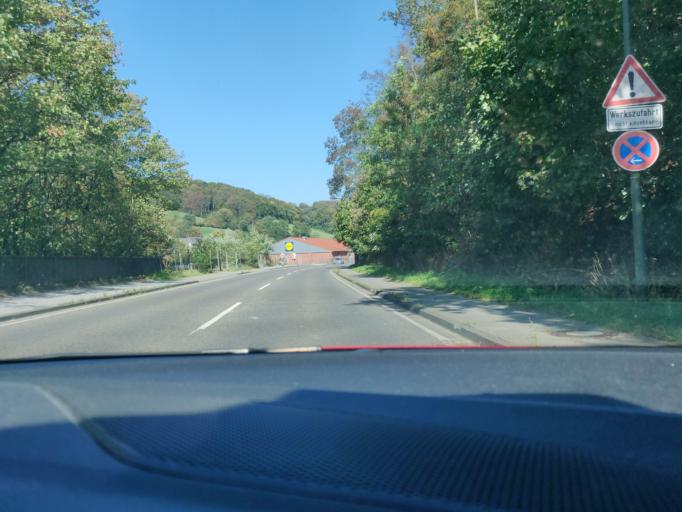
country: DE
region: North Rhine-Westphalia
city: Hattingen
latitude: 51.3588
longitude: 7.1239
